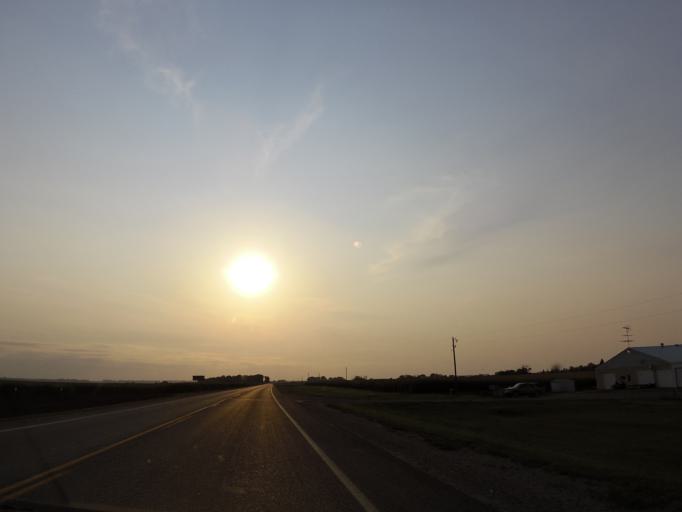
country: US
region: North Dakota
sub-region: Traill County
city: Mayville
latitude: 47.4982
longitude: -97.3895
